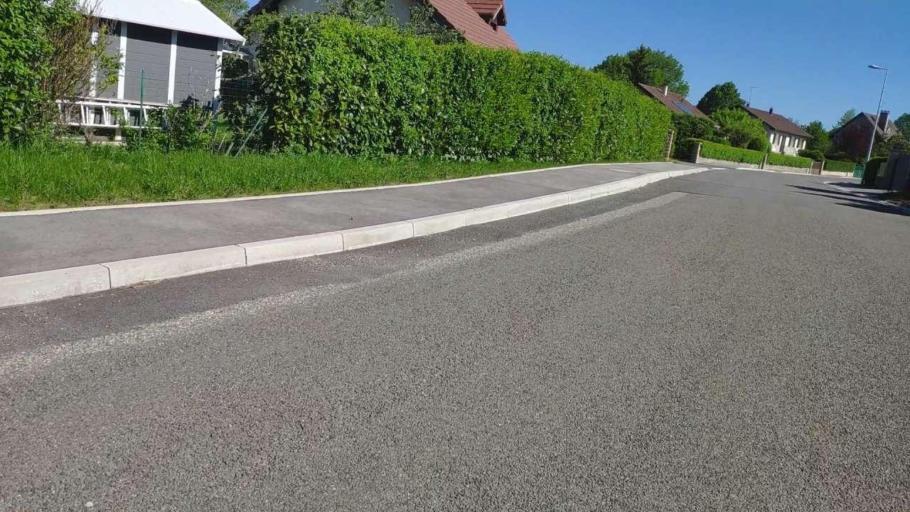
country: FR
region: Franche-Comte
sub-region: Departement du Jura
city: Perrigny
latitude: 46.6857
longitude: 5.6646
